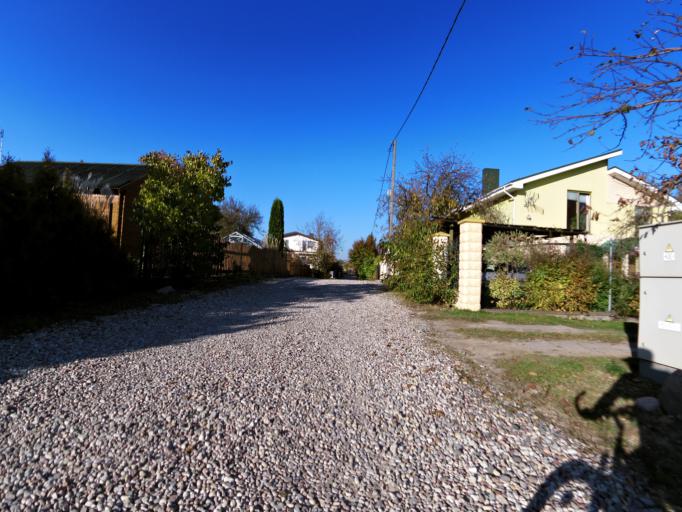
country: LT
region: Vilnius County
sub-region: Vilnius
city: Fabijoniskes
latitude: 54.7423
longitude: 25.2599
